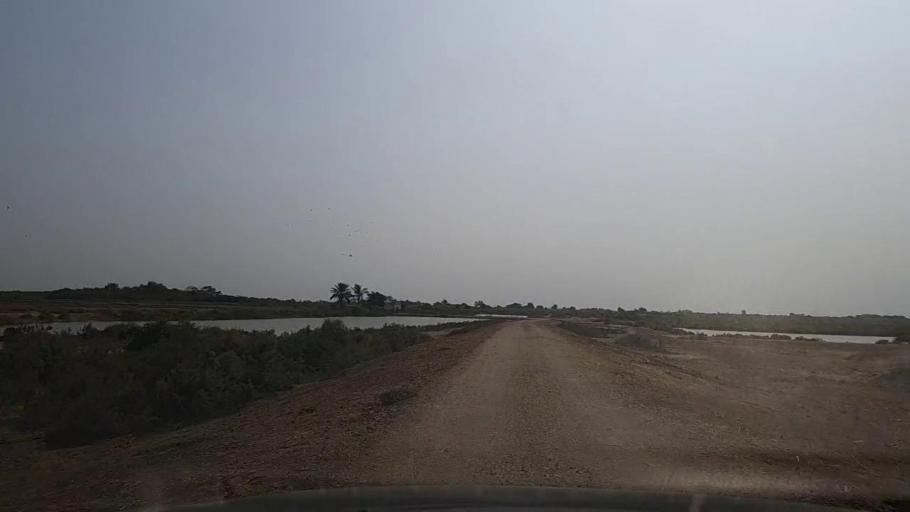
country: PK
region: Sindh
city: Thatta
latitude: 24.5711
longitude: 67.9169
